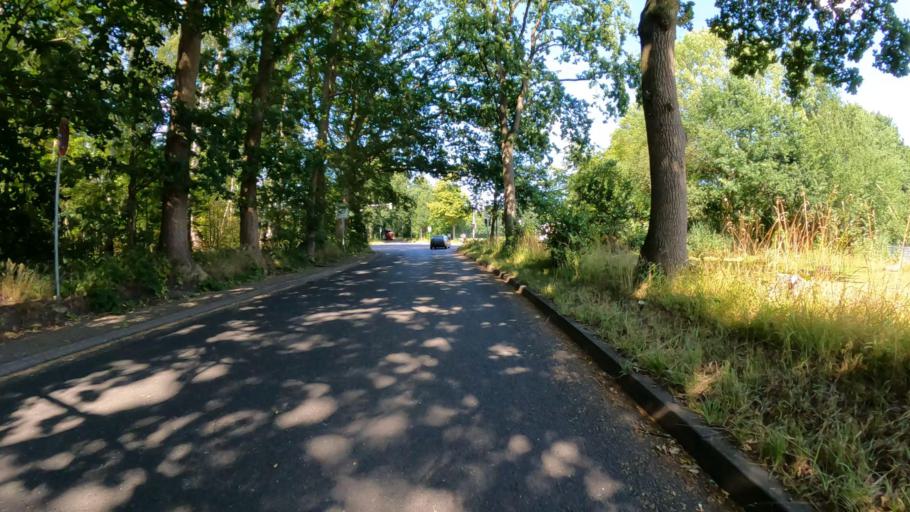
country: DE
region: Schleswig-Holstein
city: Halstenbek
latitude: 53.6213
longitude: 9.8623
